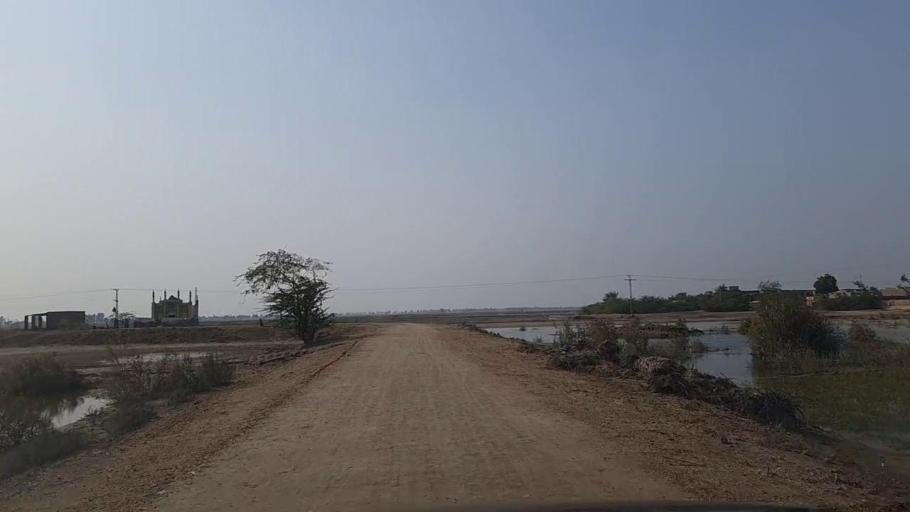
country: PK
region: Sindh
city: Daur
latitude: 26.3915
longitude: 68.4201
